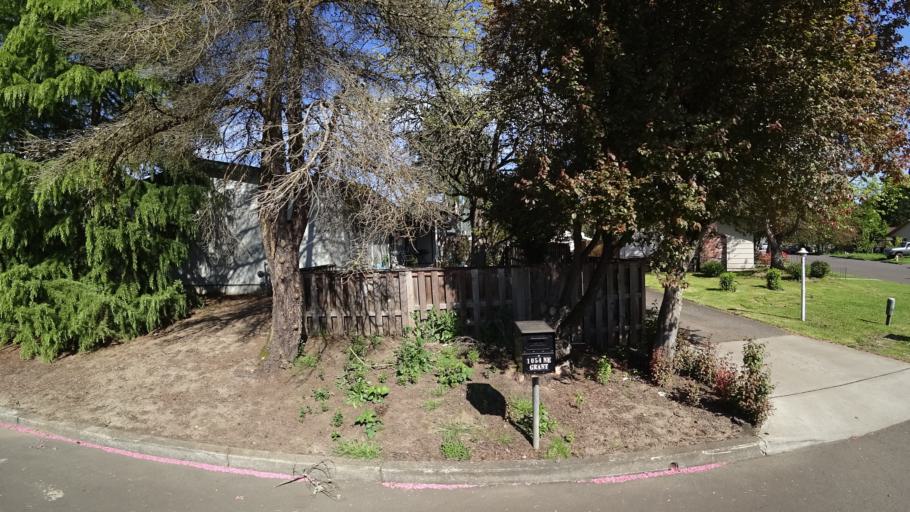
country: US
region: Oregon
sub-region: Washington County
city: Hillsboro
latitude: 45.5274
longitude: -122.9721
